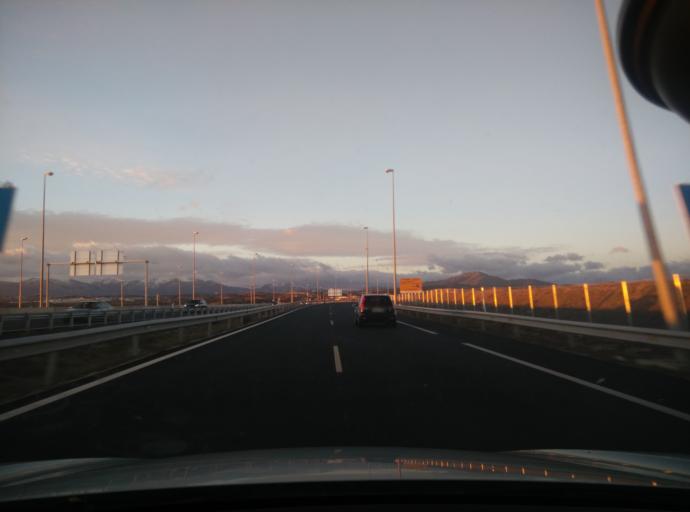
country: ES
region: Madrid
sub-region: Provincia de Madrid
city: Tres Cantos
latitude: 40.6210
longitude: -3.7300
